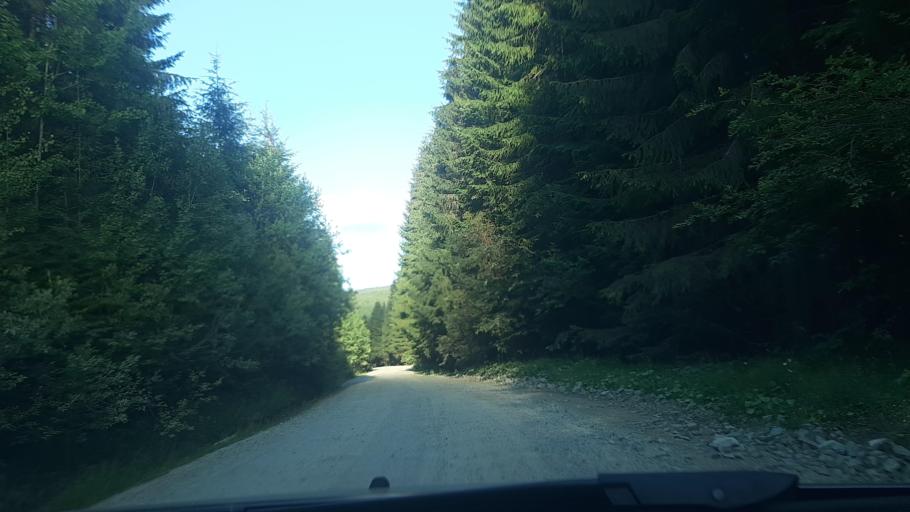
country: RO
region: Alba
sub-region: Comuna Sugag
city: Sugag
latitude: 45.5854
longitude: 23.6140
